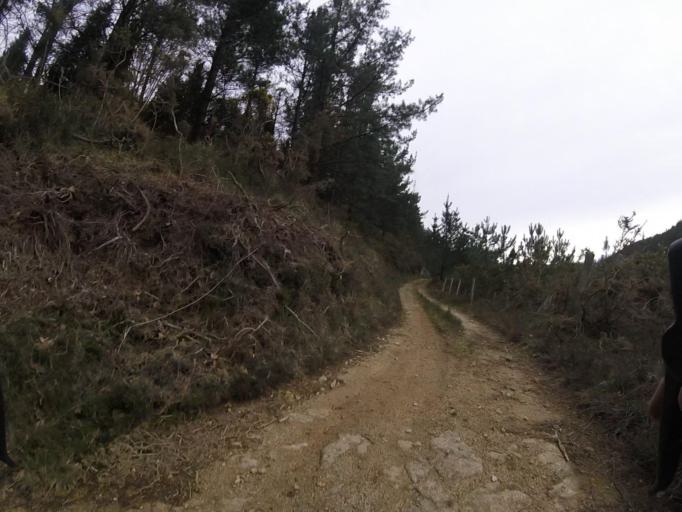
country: ES
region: Navarre
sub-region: Provincia de Navarra
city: Bera
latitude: 43.2914
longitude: -1.7340
